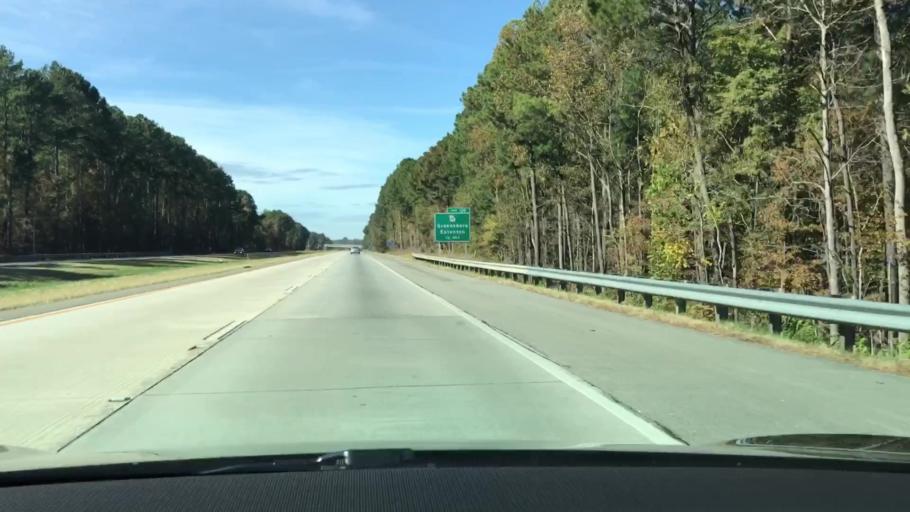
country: US
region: Georgia
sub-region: Greene County
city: Greensboro
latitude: 33.5467
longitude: -83.1904
